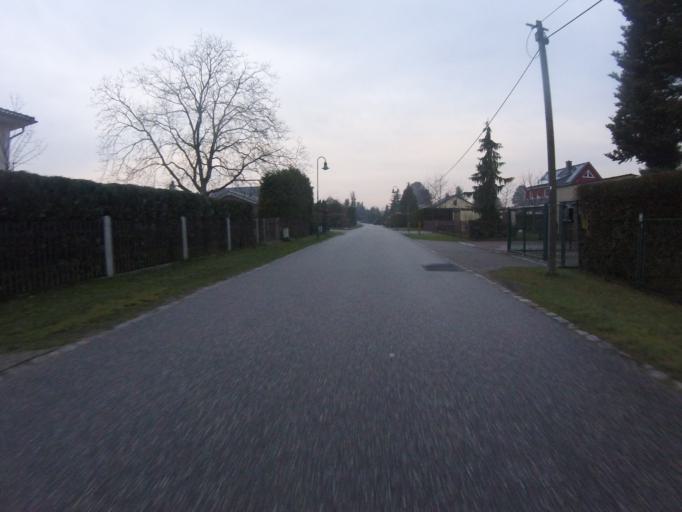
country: DE
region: Brandenburg
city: Konigs Wusterhausen
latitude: 52.2883
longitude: 13.6783
